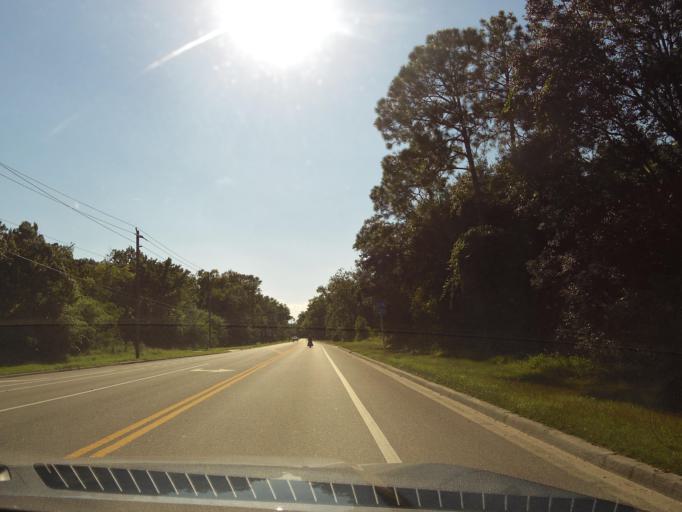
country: US
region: Florida
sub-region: Saint Johns County
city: Saint Augustine
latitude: 29.8872
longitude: -81.3550
